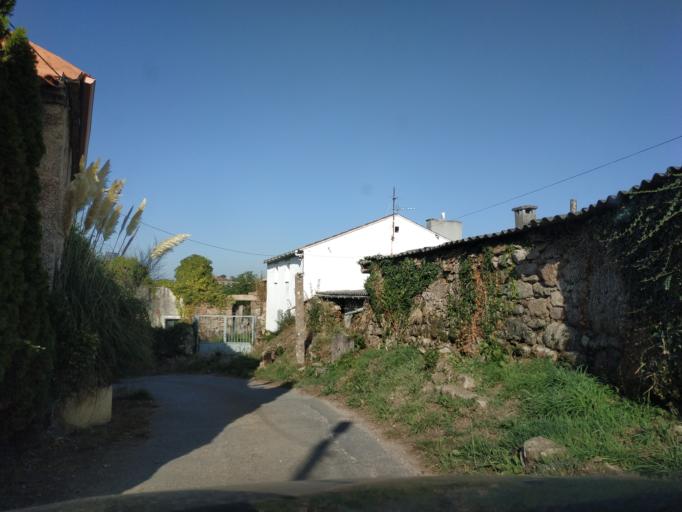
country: ES
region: Galicia
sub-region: Provincia da Coruna
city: A Coruna
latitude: 43.3319
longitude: -8.4036
